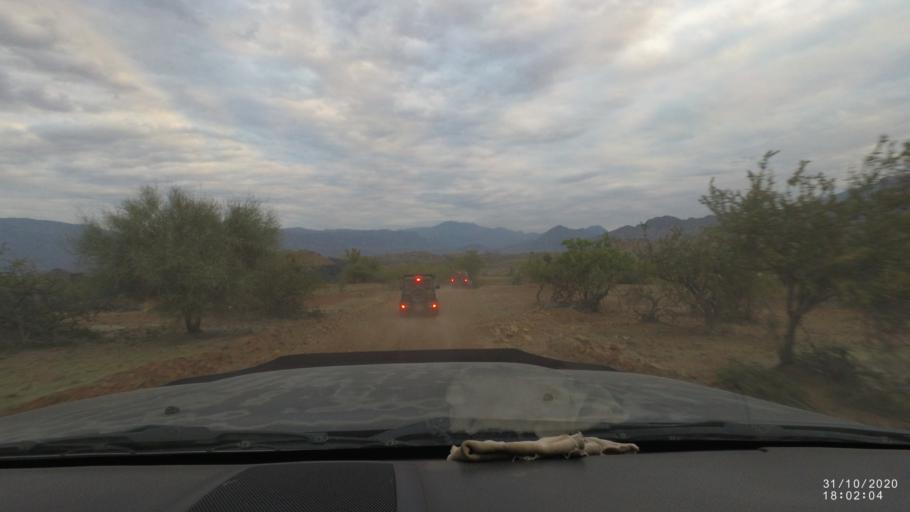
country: BO
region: Chuquisaca
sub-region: Provincia Zudanez
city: Mojocoya
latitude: -18.6654
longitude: -64.5290
